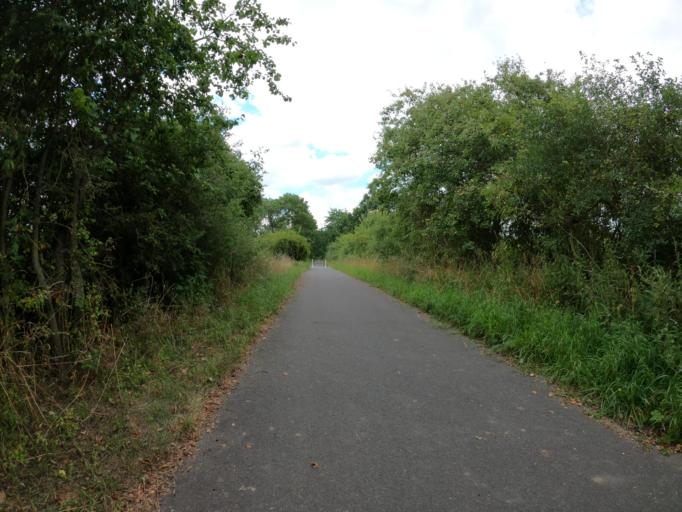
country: DE
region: Mecklenburg-Vorpommern
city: Woldegk
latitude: 53.3650
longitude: 13.5897
